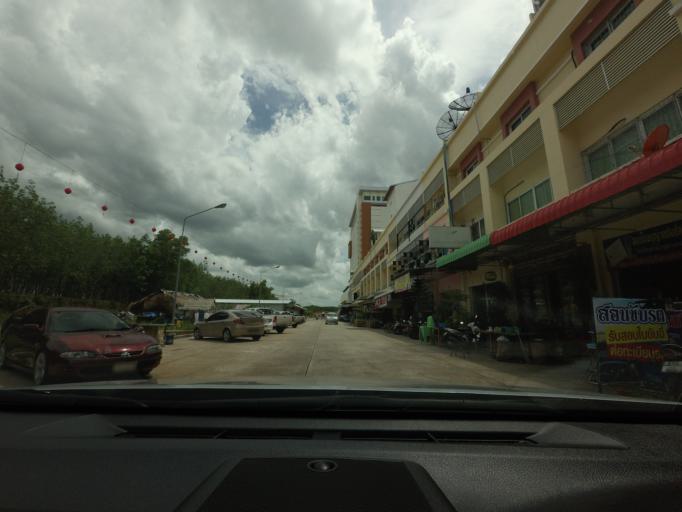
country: TH
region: Songkhla
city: Sadao
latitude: 6.5284
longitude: 100.4172
